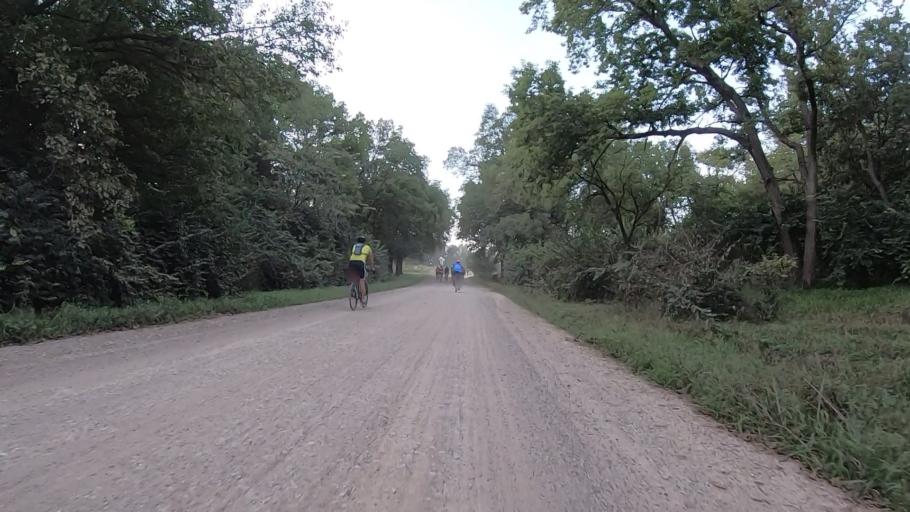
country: US
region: Kansas
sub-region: Marshall County
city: Marysville
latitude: 39.8322
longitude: -96.6649
